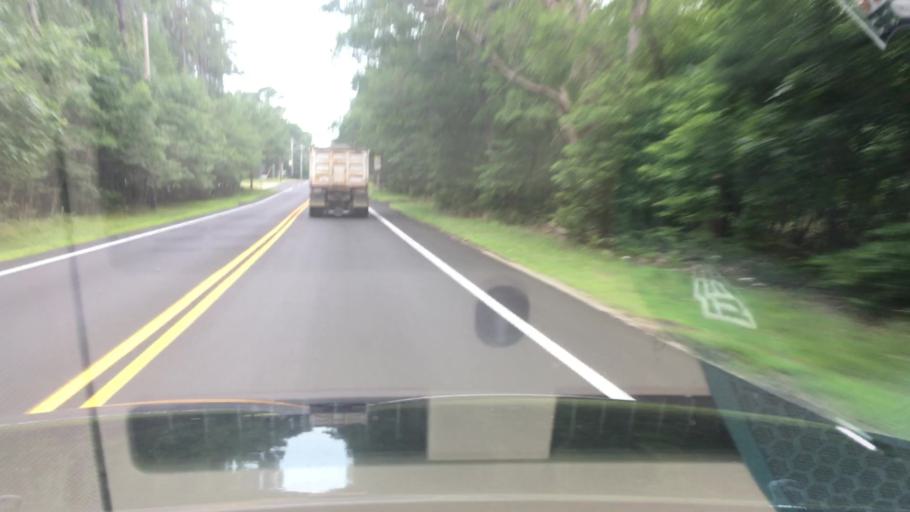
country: US
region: New Jersey
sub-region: Ocean County
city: Lakehurst
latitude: 40.0574
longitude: -74.3513
